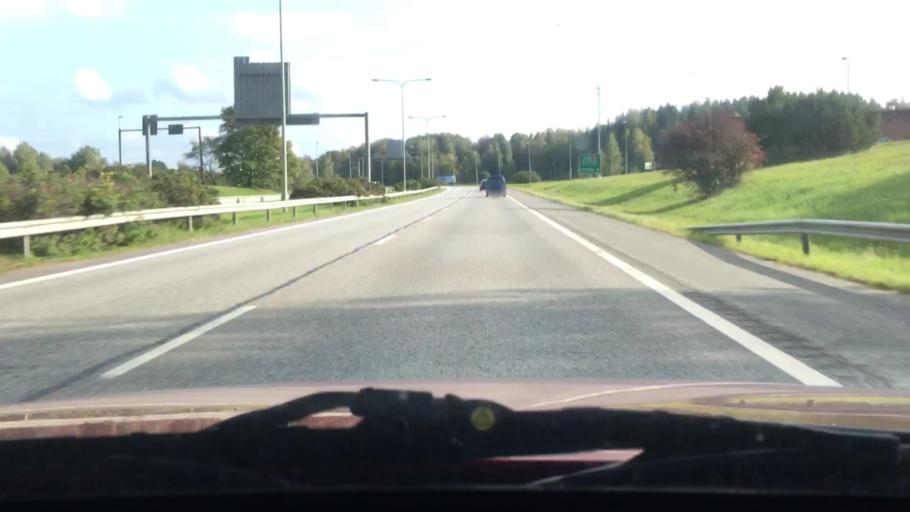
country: FI
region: Varsinais-Suomi
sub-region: Turku
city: Raisio
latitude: 60.4822
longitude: 22.1810
